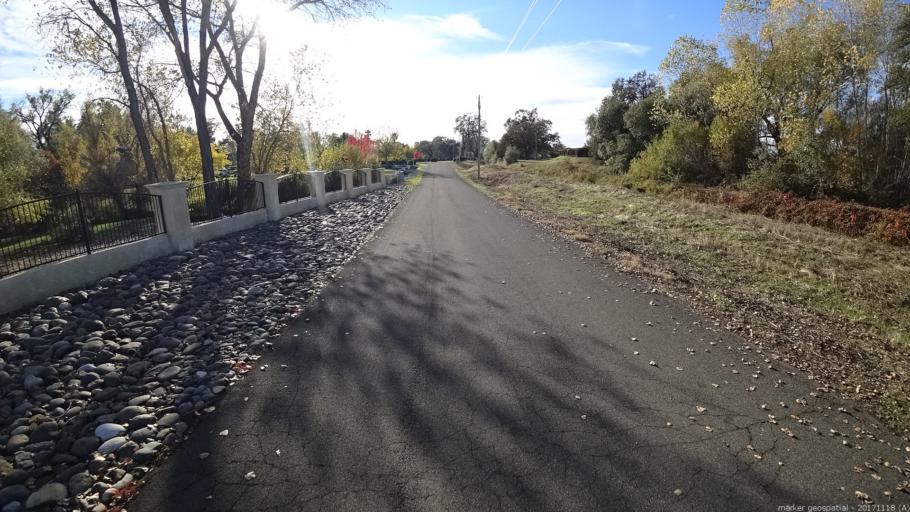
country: US
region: California
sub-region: Shasta County
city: Cottonwood
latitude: 40.3754
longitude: -122.3385
